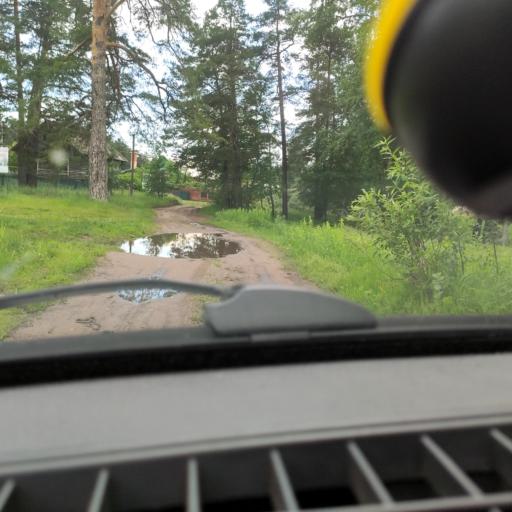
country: RU
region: Samara
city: Povolzhskiy
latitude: 53.6356
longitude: 49.6846
